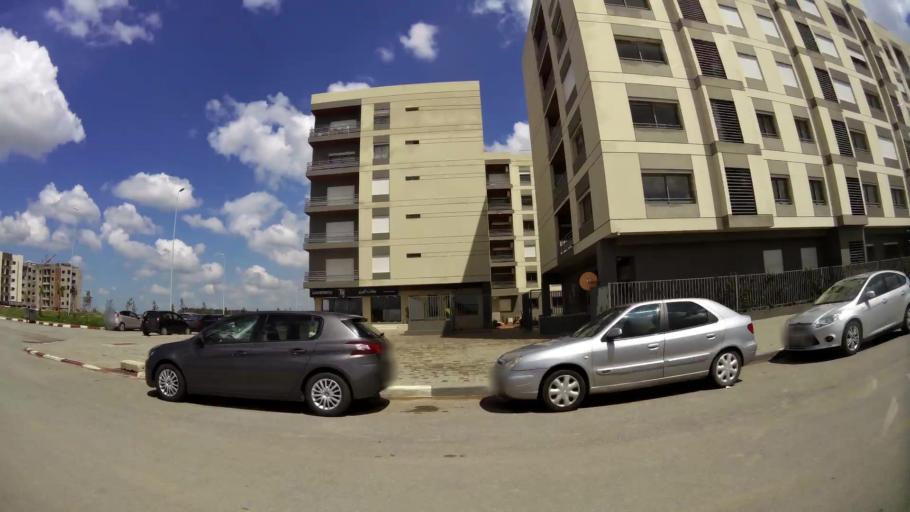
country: MA
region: Chaouia-Ouardigha
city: Nouaseur
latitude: 33.3885
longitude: -7.5604
